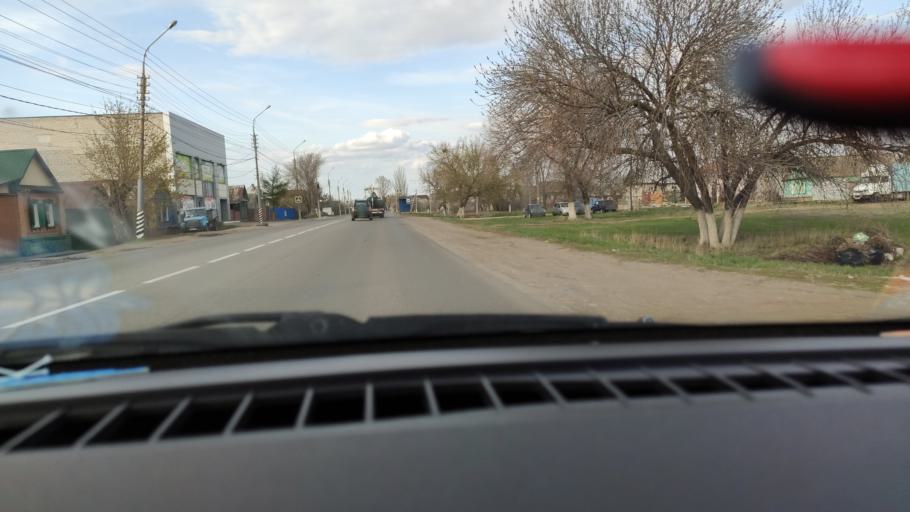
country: RU
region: Saratov
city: Privolzhskiy
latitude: 51.4301
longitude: 46.0538
